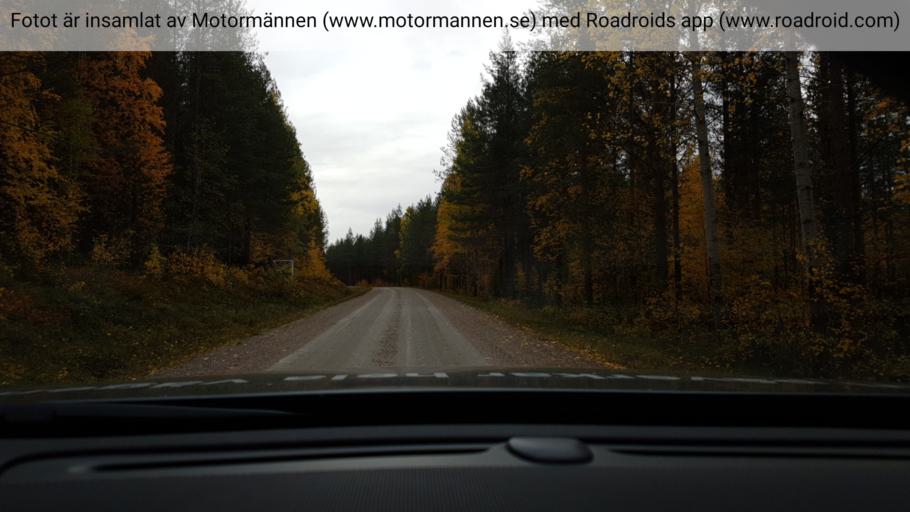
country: SE
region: Norrbotten
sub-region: Overkalix Kommun
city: OEverkalix
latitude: 66.2802
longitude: 22.9796
